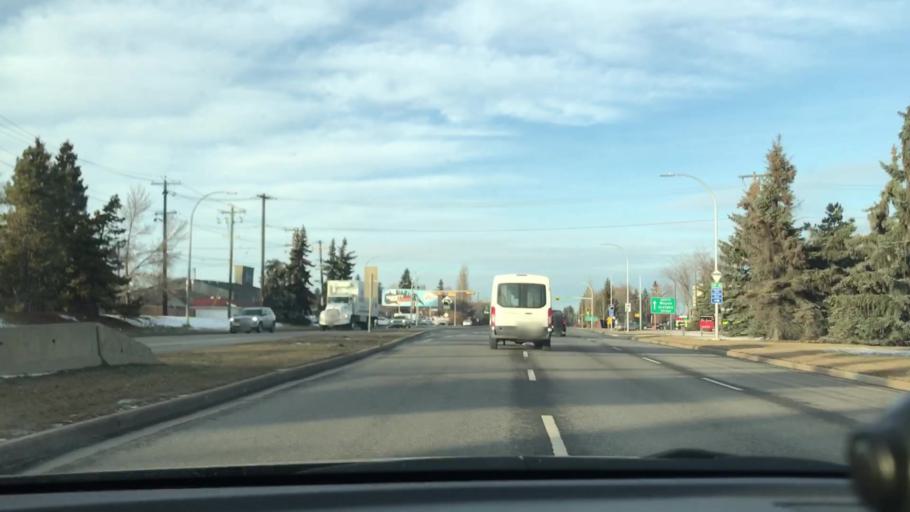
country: CA
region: Alberta
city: Edmonton
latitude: 53.5397
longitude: -113.4434
